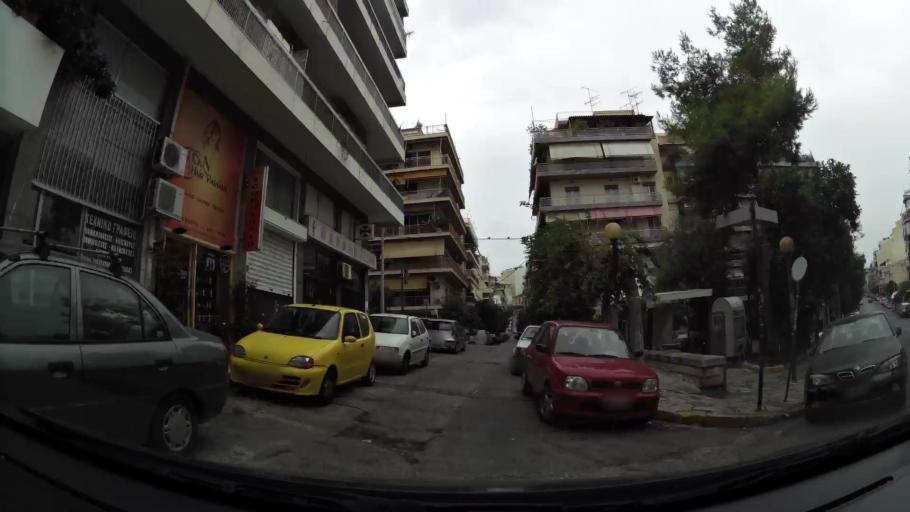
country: GR
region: Attica
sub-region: Nomos Attikis
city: Piraeus
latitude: 37.9310
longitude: 23.6425
